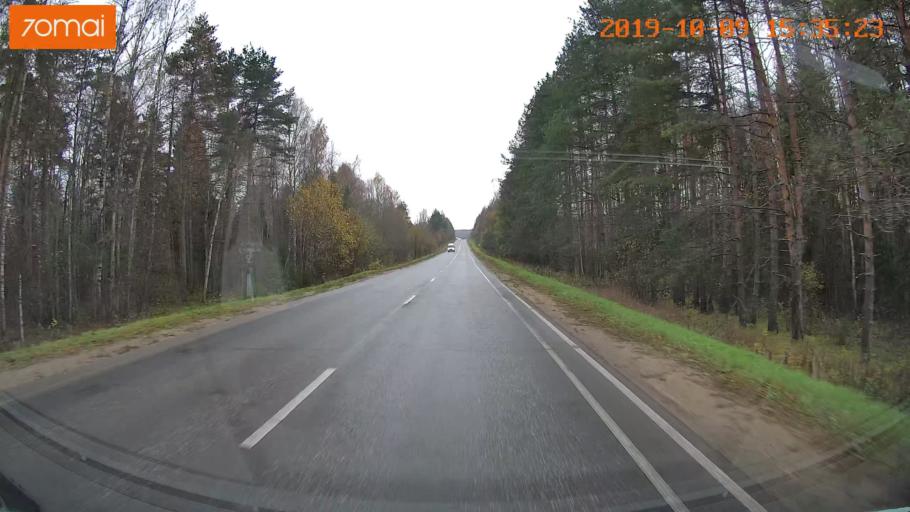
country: RU
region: Kostroma
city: Oktyabr'skiy
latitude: 57.9326
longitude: 41.2283
